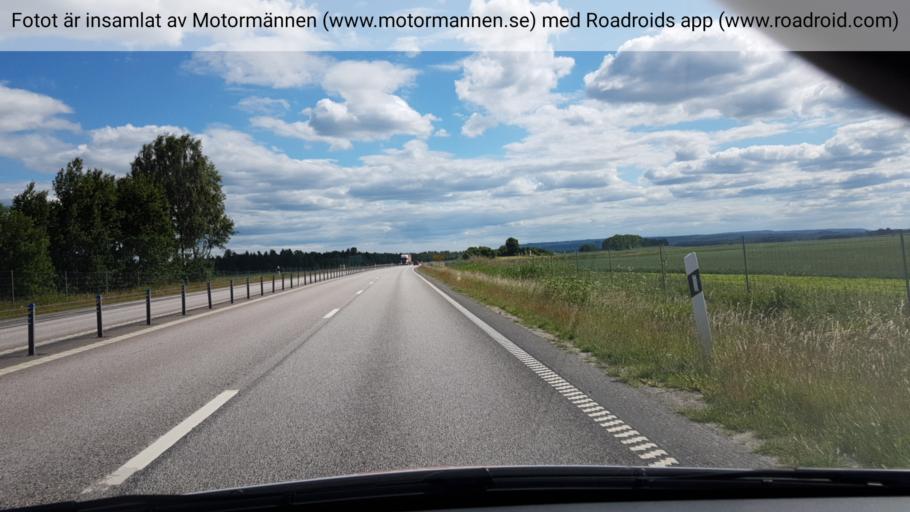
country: SE
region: Vaestra Goetaland
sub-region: Mariestads Kommun
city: Mariestad
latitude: 58.5864
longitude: 13.8007
